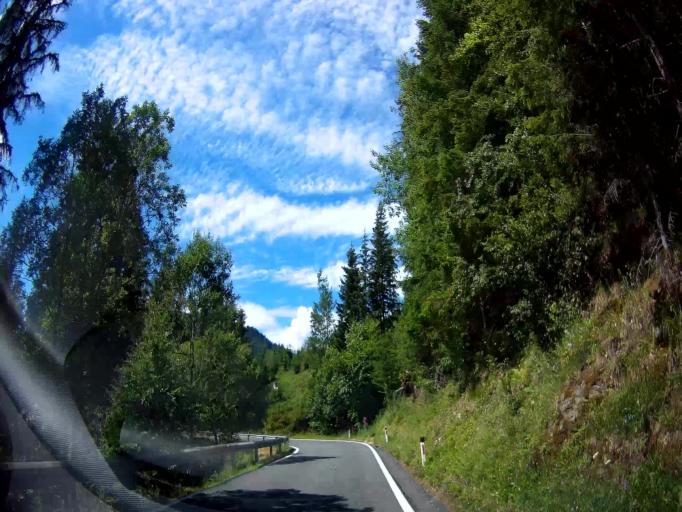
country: AT
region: Carinthia
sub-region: Politischer Bezirk Sankt Veit an der Glan
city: Glodnitz
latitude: 46.9216
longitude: 14.0558
